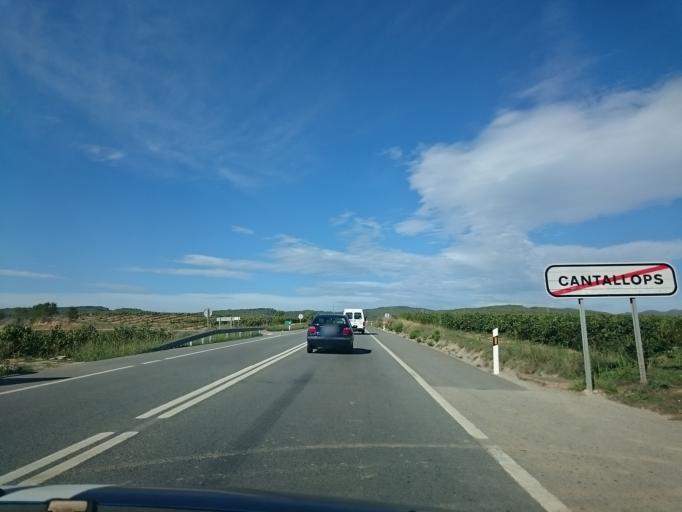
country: ES
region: Catalonia
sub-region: Provincia de Barcelona
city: Avinyonet del Penedes
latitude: 41.3715
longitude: 1.8045
